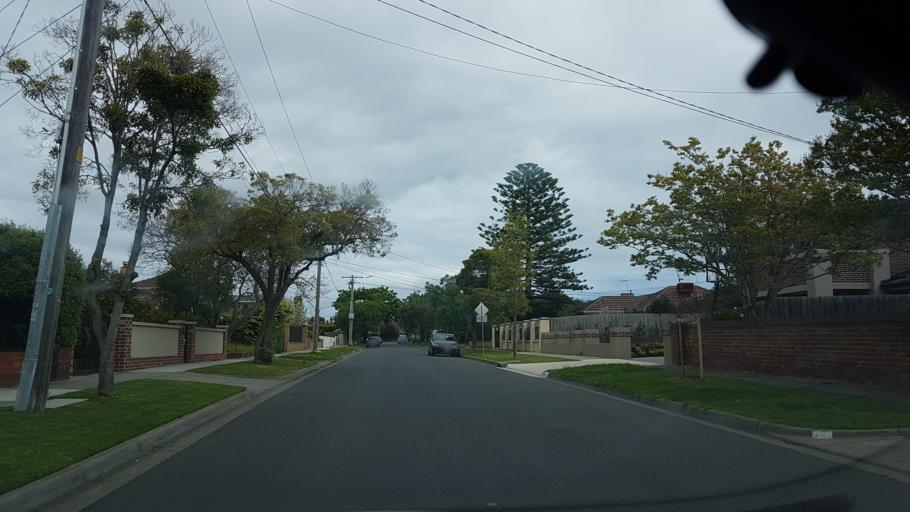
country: AU
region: Victoria
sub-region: Glen Eira
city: Bentleigh
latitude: -37.9233
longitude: 145.0296
